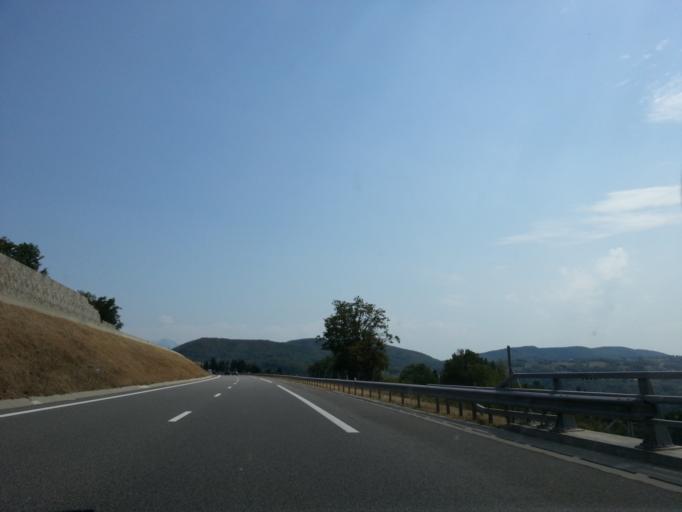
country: FR
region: Rhone-Alpes
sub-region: Departement de la Haute-Savoie
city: Cruseilles
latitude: 46.0304
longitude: 6.0915
